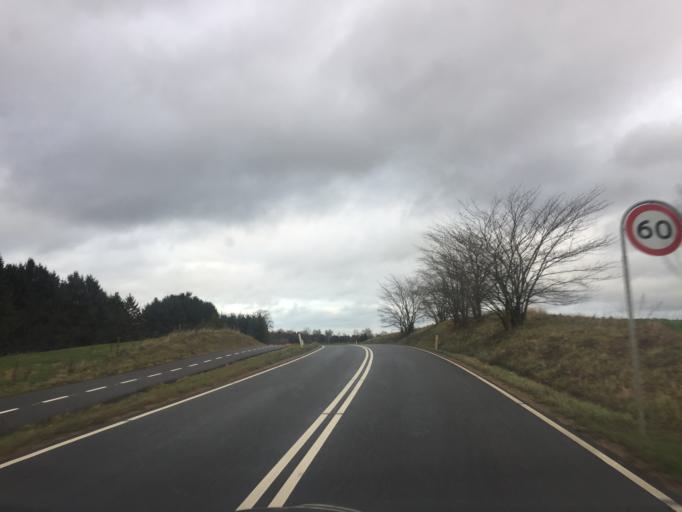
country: DK
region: Zealand
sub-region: Soro Kommune
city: Stenlille
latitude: 55.5923
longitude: 11.6738
